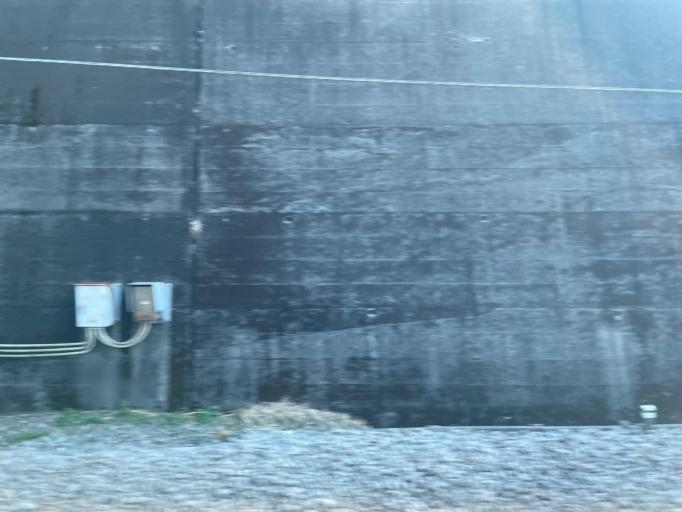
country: JP
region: Kanagawa
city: Kamakura
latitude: 35.3710
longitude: 139.5611
